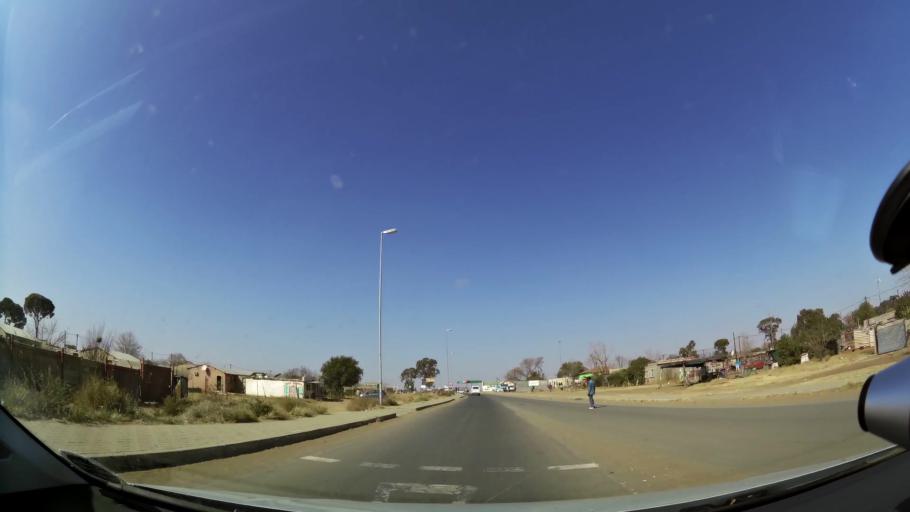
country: ZA
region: Orange Free State
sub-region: Mangaung Metropolitan Municipality
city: Bloemfontein
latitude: -29.1633
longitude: 26.2806
